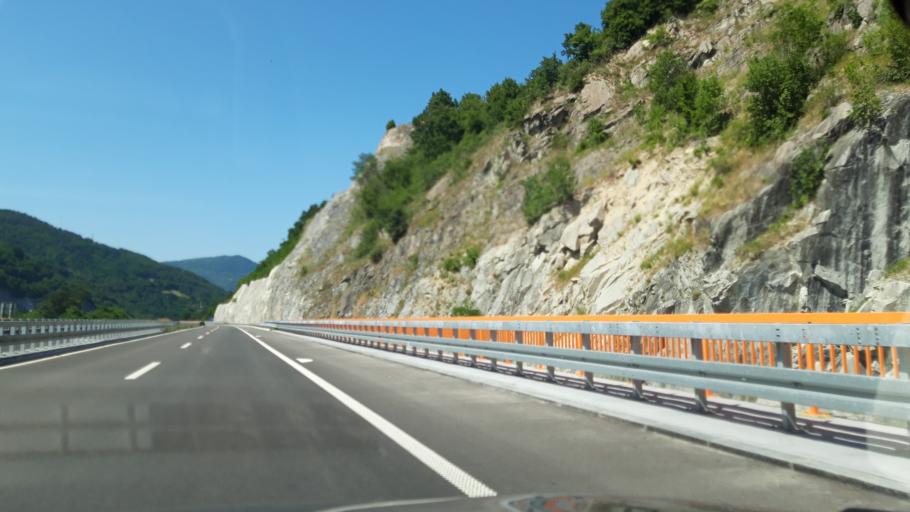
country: RS
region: Central Serbia
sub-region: Pcinjski Okrug
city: Vladicin Han
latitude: 42.7609
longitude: 22.0860
